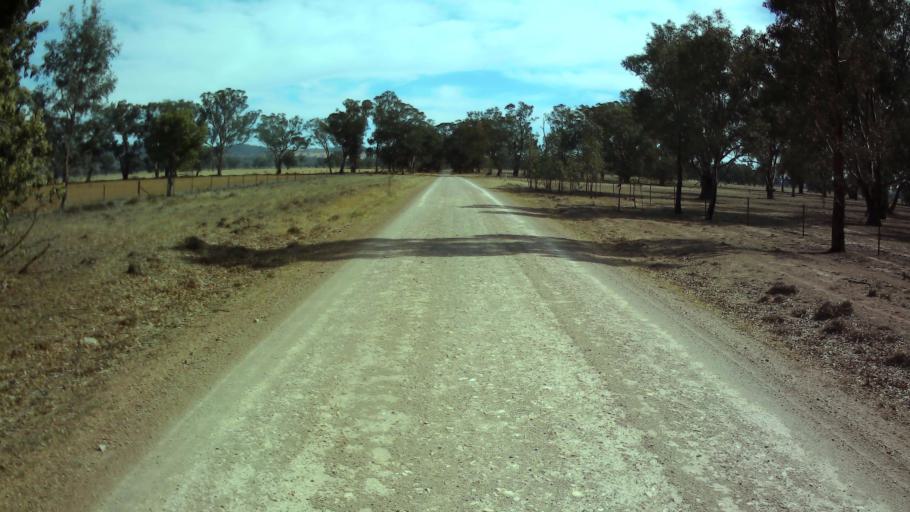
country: AU
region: New South Wales
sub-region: Weddin
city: Grenfell
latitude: -33.7015
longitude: 148.3021
